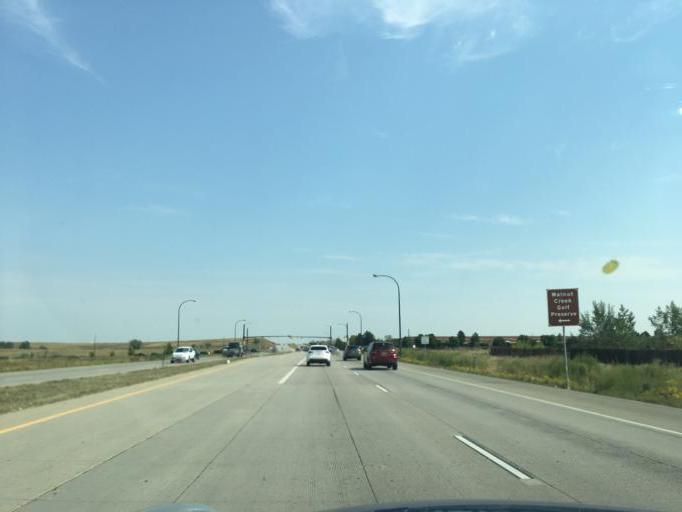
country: US
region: Colorado
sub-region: Broomfield County
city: Broomfield
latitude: 39.8898
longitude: -105.0960
